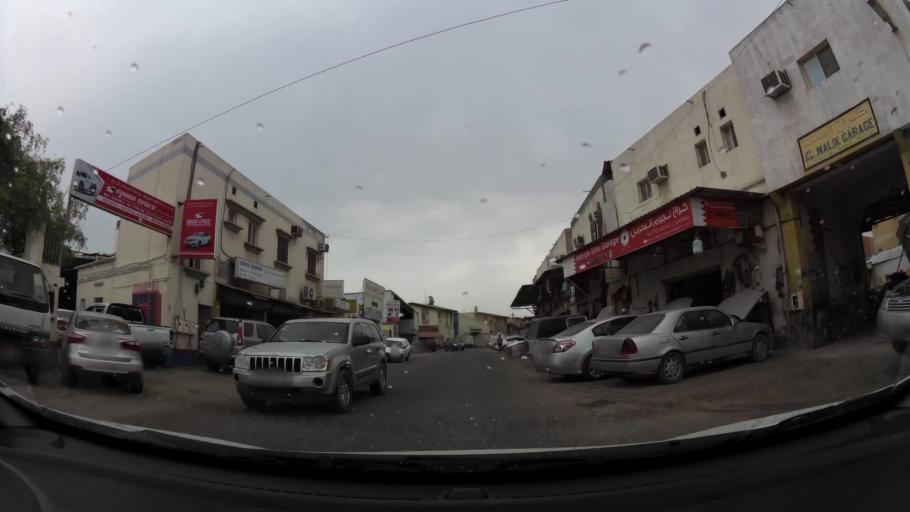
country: BH
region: Northern
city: Madinat `Isa
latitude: 26.1829
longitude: 50.5274
